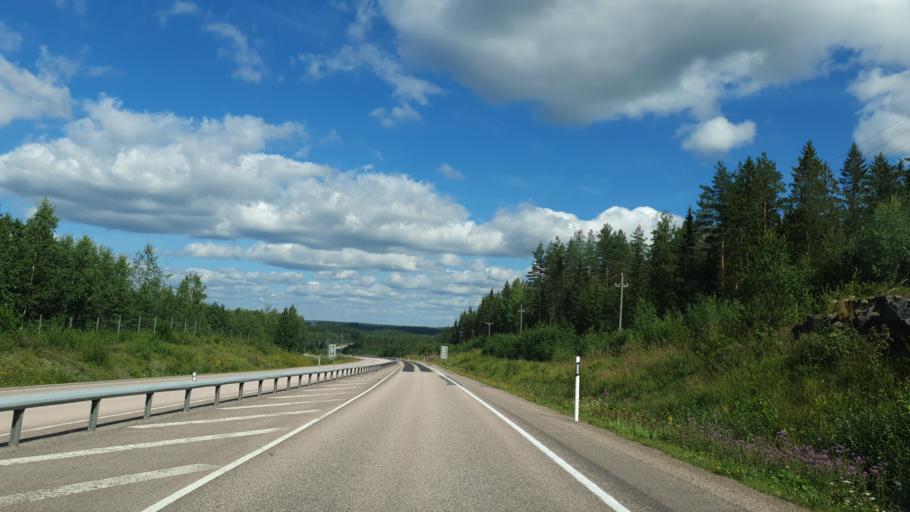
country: FI
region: Central Finland
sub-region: Jaemsae
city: Jaemsae
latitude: 61.7893
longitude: 24.9300
